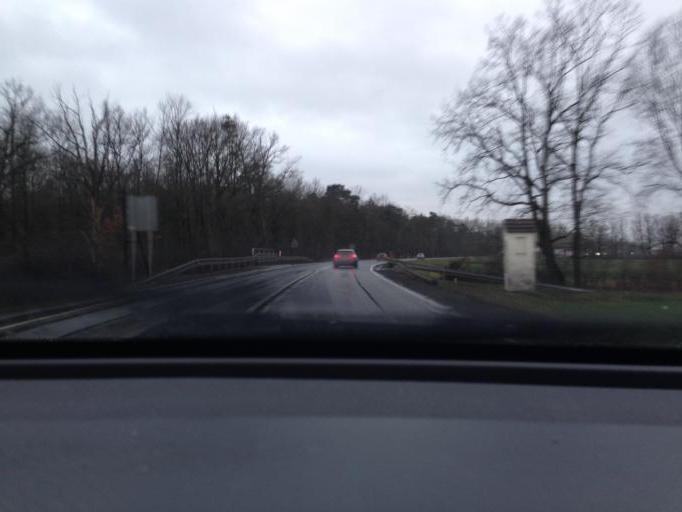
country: PL
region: Opole Voivodeship
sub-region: Powiat opolski
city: Wegry
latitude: 50.7075
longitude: 17.9846
